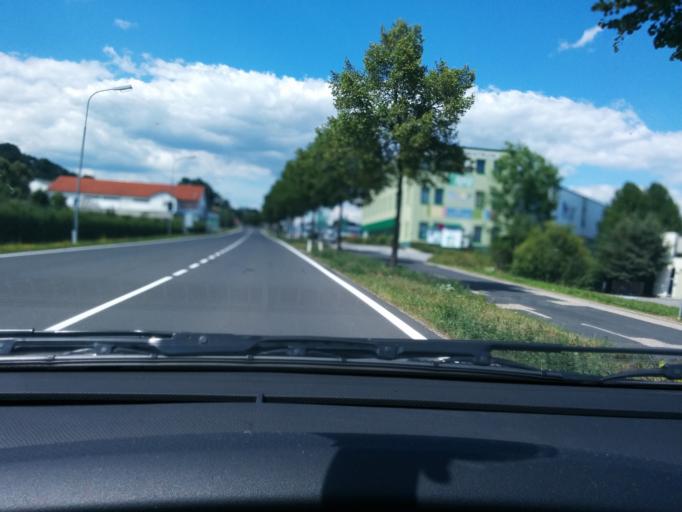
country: AT
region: Styria
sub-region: Politischer Bezirk Hartberg-Fuerstenfeld
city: Hartberg
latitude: 47.2882
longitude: 15.9794
